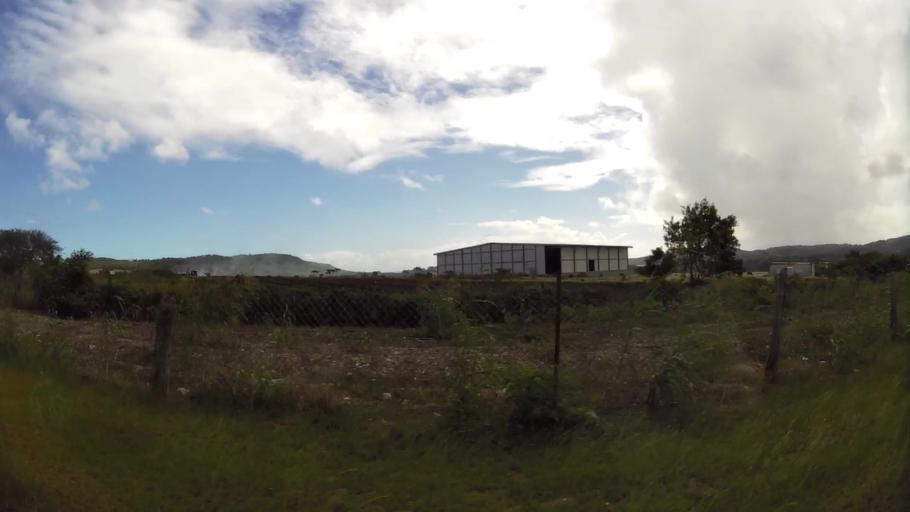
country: AG
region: Saint Paul
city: Liberta
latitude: 17.0532
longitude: -61.7465
